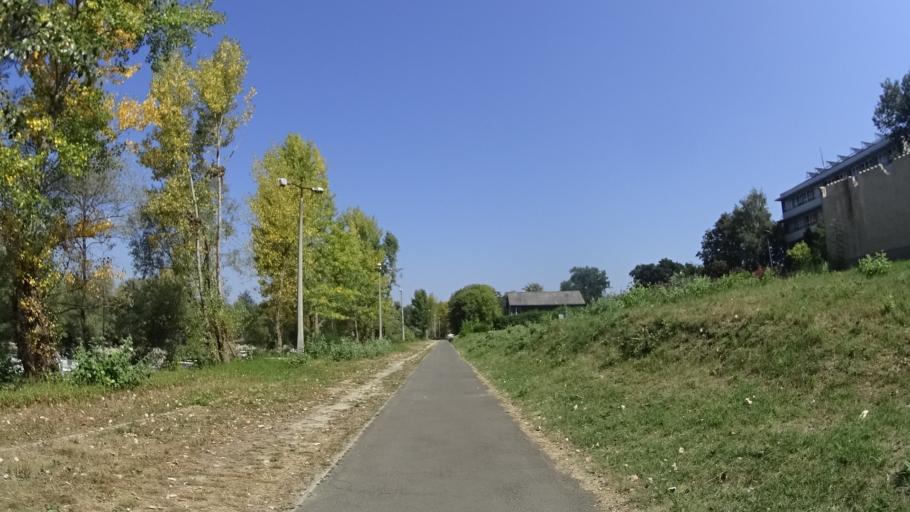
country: HU
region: Pest
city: Szodliget
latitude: 47.7299
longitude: 19.1339
